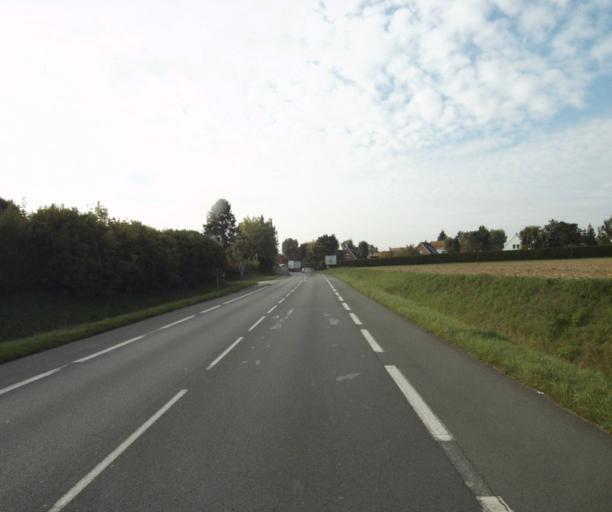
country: FR
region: Nord-Pas-de-Calais
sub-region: Departement du Nord
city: Wattignies
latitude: 50.5851
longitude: 3.0340
